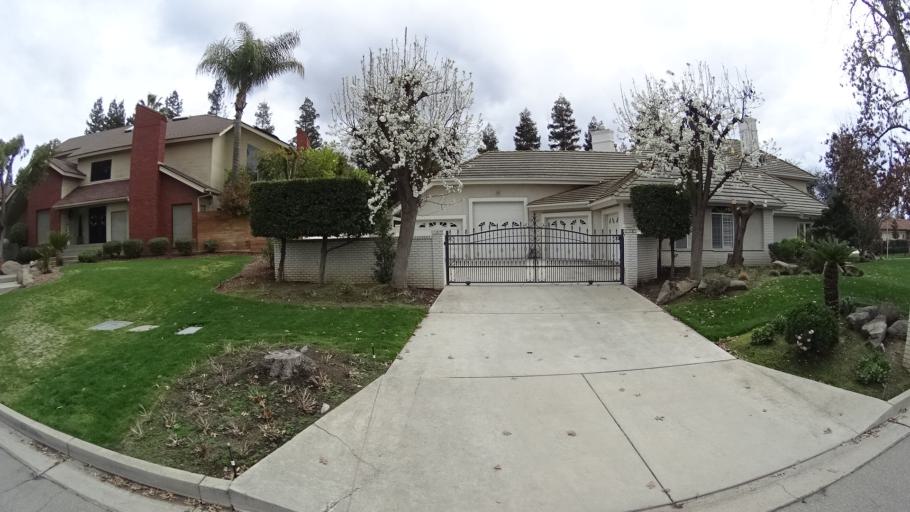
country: US
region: California
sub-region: Fresno County
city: Fresno
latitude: 36.8487
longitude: -119.8370
